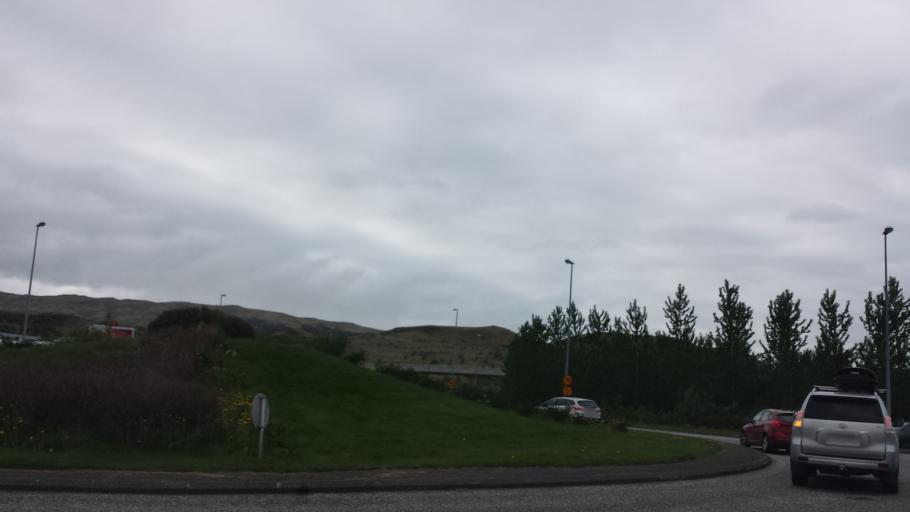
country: IS
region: Capital Region
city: Mosfellsbaer
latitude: 64.1657
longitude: -21.6928
